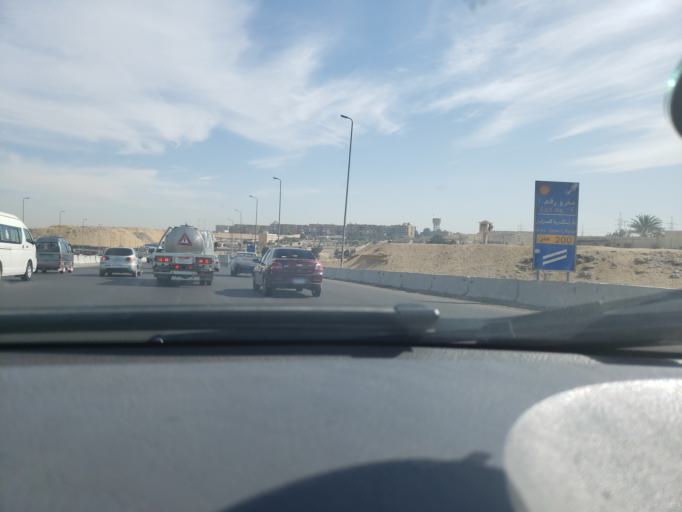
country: EG
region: Al Jizah
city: Al Jizah
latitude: 29.9970
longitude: 31.1050
